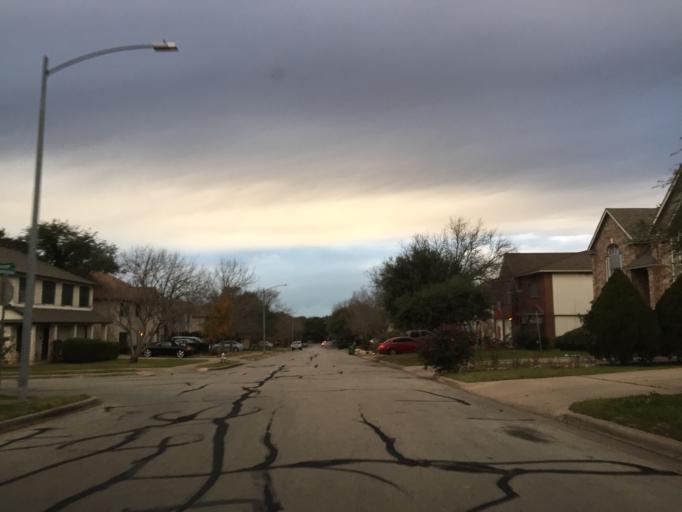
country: US
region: Texas
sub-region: Williamson County
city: Jollyville
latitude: 30.4491
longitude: -97.7496
